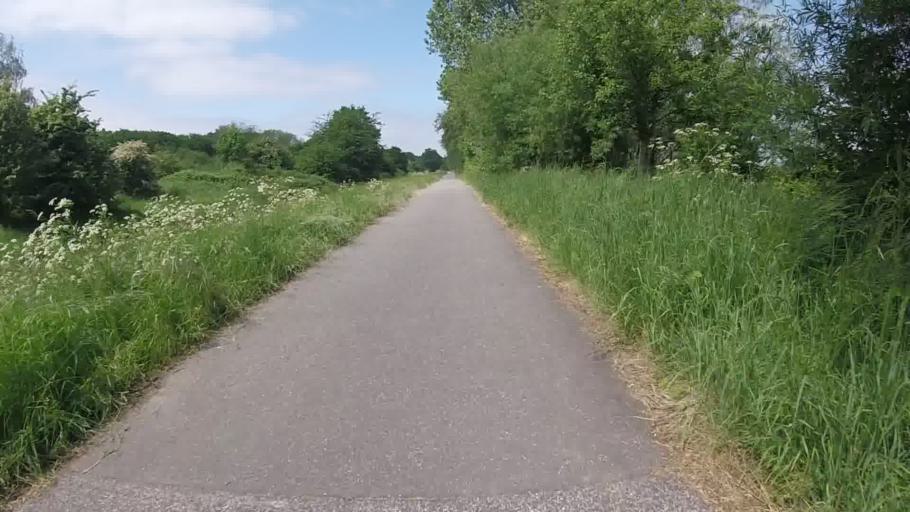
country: DE
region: Schleswig-Holstein
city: Oststeinbek
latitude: 53.4929
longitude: 10.1467
